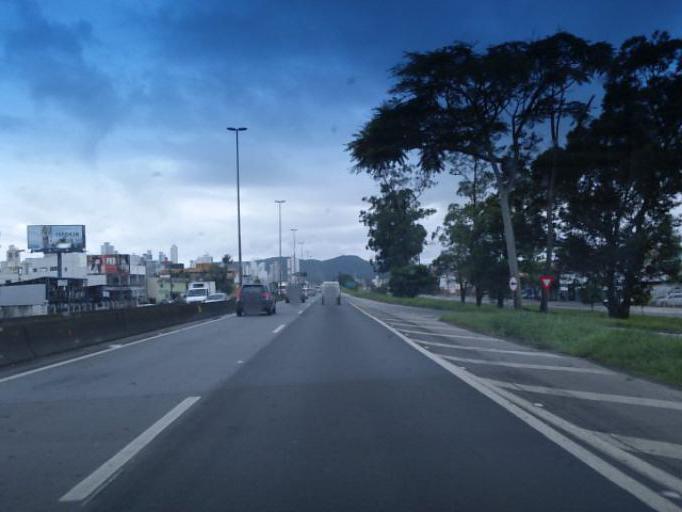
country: BR
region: Santa Catarina
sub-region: Balneario Camboriu
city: Balneario Camboriu
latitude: -27.0003
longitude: -48.6429
